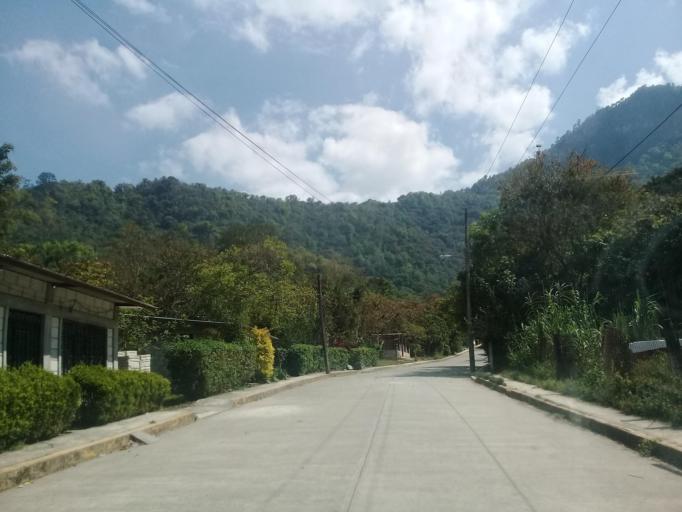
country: MX
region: Veracruz
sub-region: Tlilapan
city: Tonalixco
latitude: 18.8031
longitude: -97.0710
